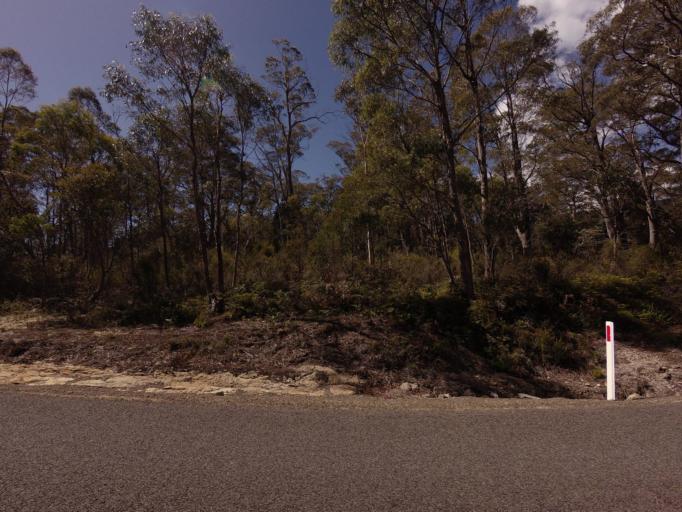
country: AU
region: Tasmania
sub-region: Break O'Day
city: St Helens
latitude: -41.6092
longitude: 148.2127
